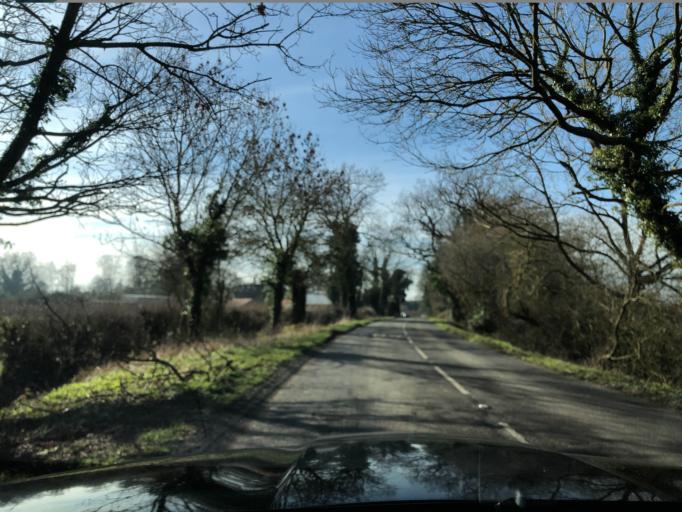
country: GB
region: England
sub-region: Solihull
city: Berkswell
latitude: 52.3983
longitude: -1.6147
